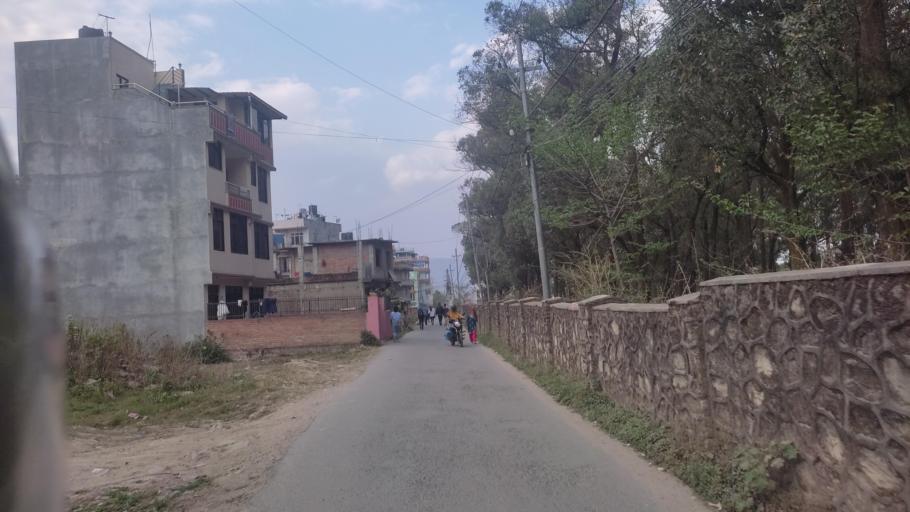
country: NP
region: Central Region
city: Kirtipur
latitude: 27.6815
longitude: 85.2816
